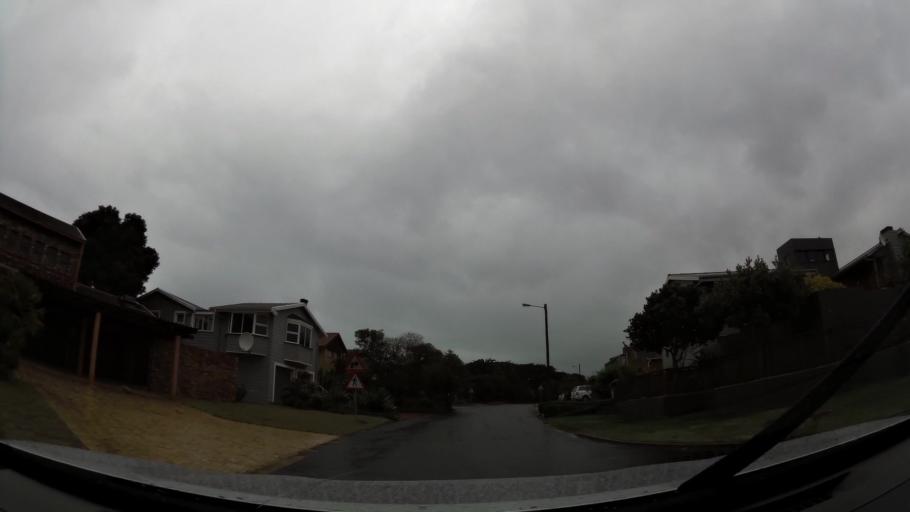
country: ZA
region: Western Cape
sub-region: Eden District Municipality
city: Mossel Bay
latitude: -34.0538
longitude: 22.2462
